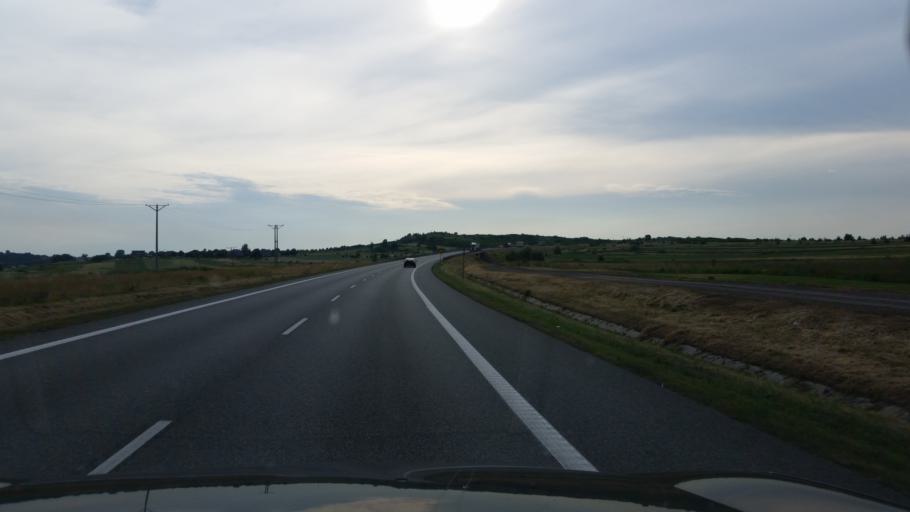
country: PL
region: Silesian Voivodeship
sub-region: Powiat bedzinski
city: Mierzecice
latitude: 50.4251
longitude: 19.1680
